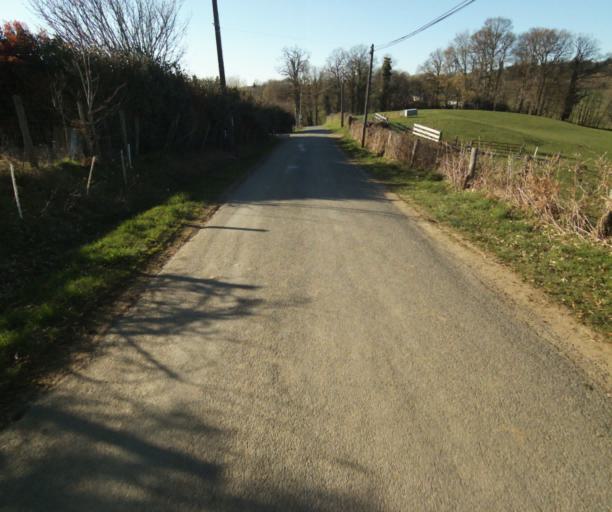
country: FR
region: Limousin
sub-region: Departement de la Correze
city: Seilhac
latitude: 45.3732
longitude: 1.7177
